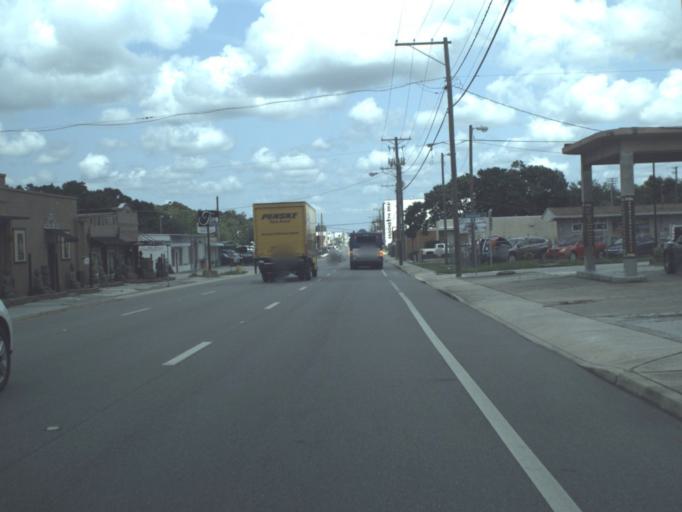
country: US
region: Florida
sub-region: Hillsborough County
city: Tampa
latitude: 27.9837
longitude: -82.4594
